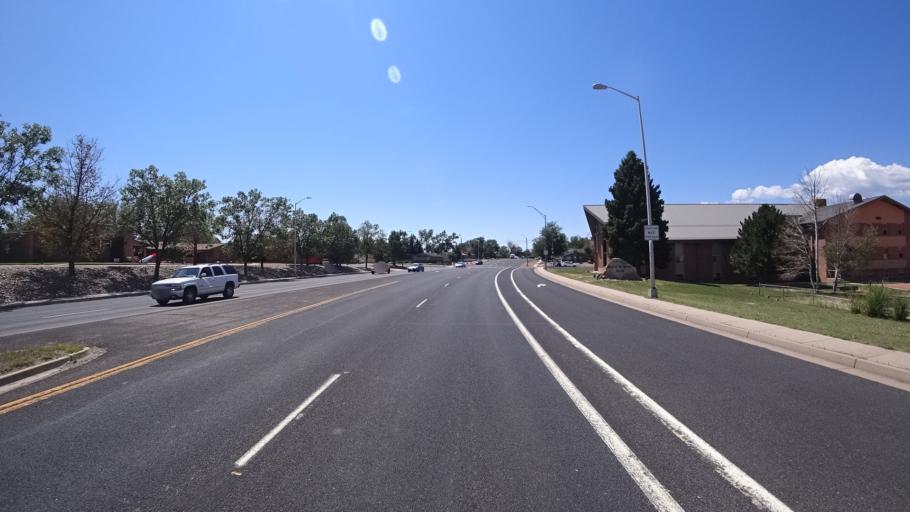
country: US
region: Colorado
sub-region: El Paso County
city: Colorado Springs
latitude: 38.8710
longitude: -104.7944
